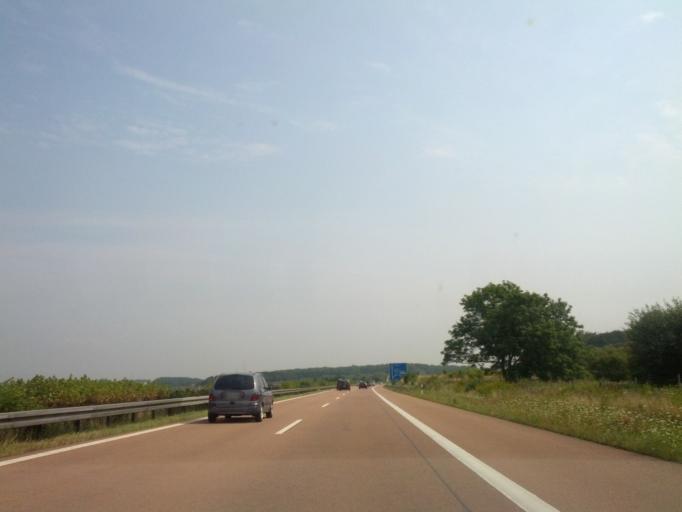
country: DE
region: Mecklenburg-Vorpommern
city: Tessin
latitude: 54.0338
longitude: 12.3970
